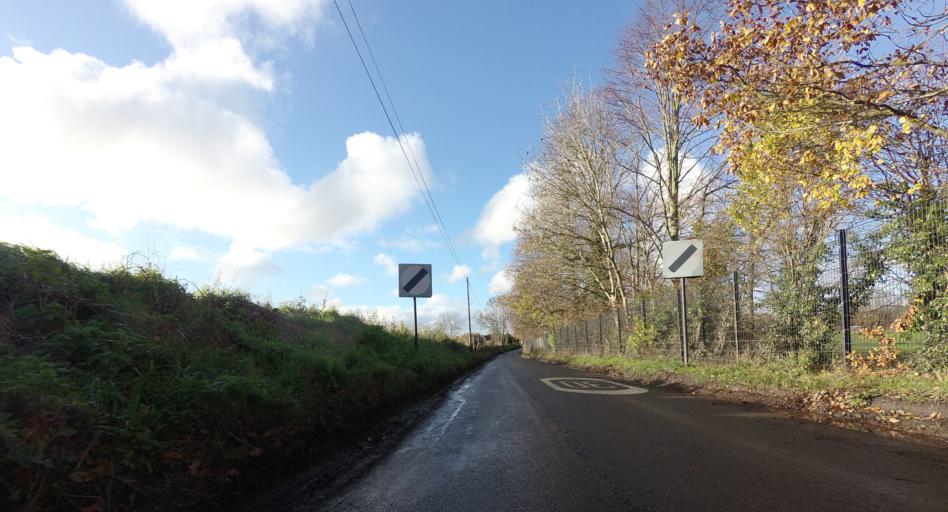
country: GB
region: England
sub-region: Kent
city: Dartford
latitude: 51.4259
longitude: 0.1945
